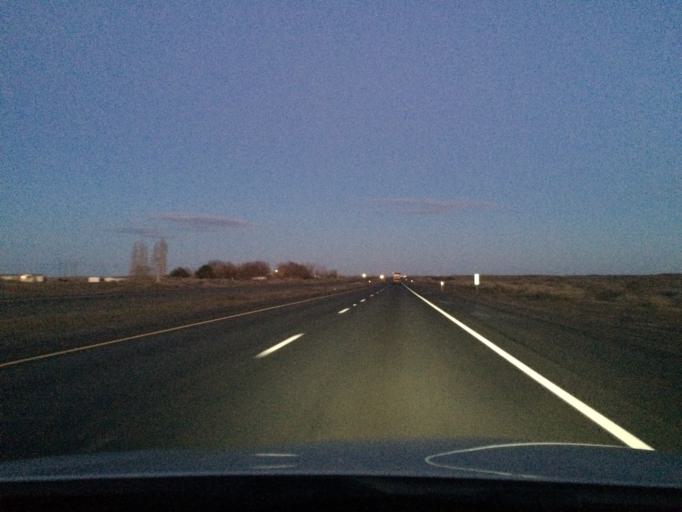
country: US
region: Washington
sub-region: Grant County
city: Cascade Valley
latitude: 47.1039
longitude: -119.4228
